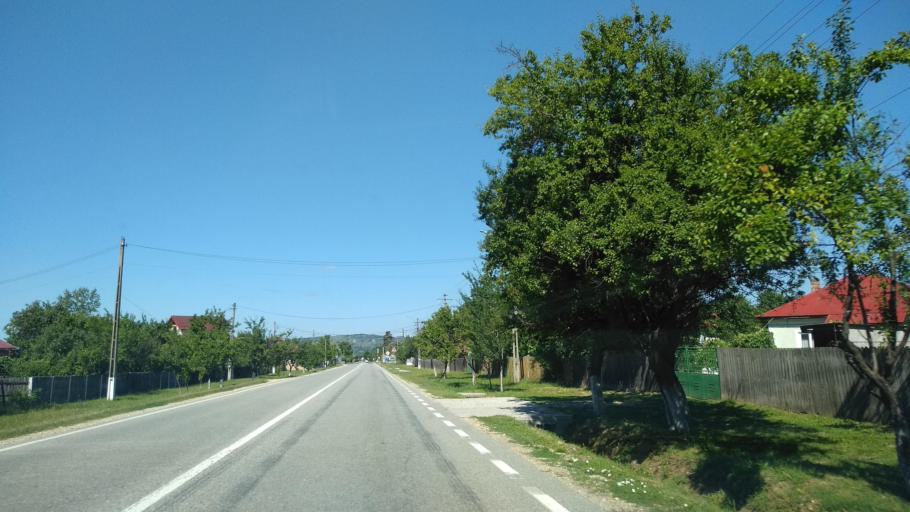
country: RO
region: Gorj
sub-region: Comuna Baia de Fier
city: Baia de Fier
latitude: 45.1385
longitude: 23.7404
